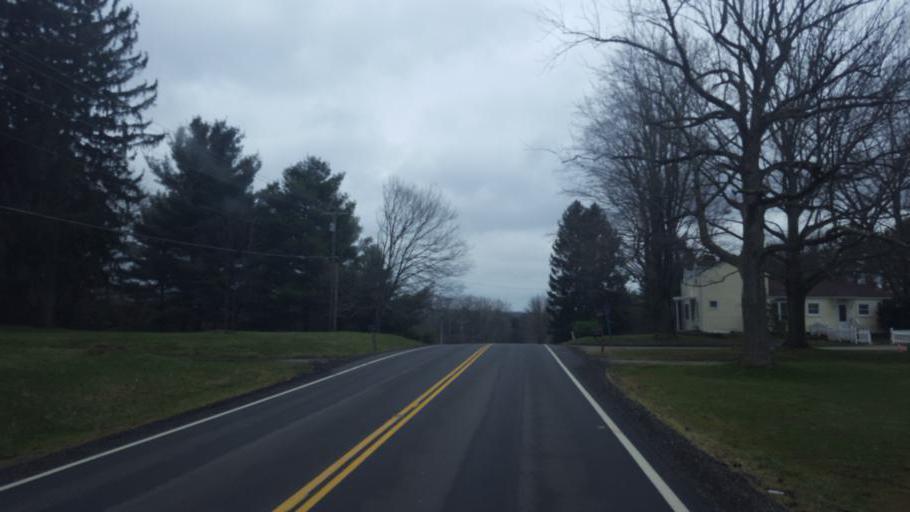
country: US
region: Ohio
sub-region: Medina County
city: Medina
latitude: 41.1065
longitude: -81.8113
